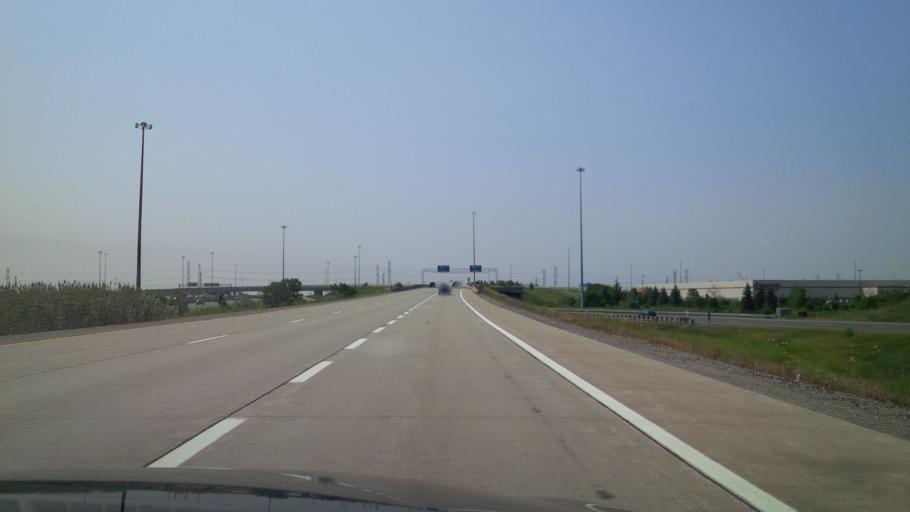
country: CA
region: Ontario
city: Concord
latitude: 43.7892
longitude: -79.5397
